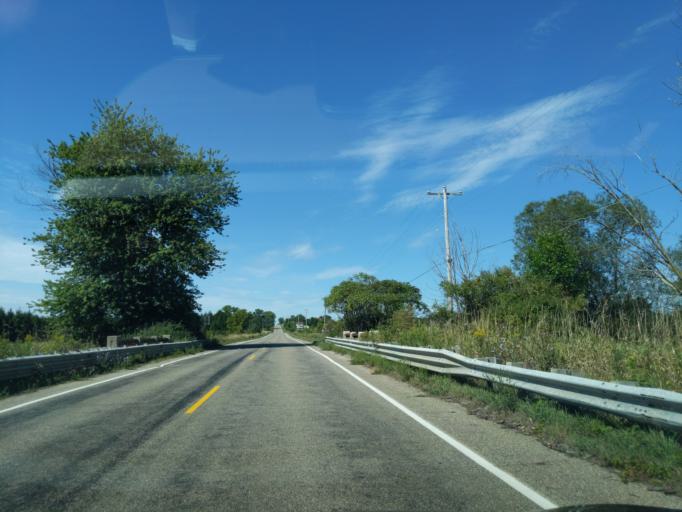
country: US
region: Michigan
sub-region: Eaton County
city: Potterville
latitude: 42.6259
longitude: -84.7739
